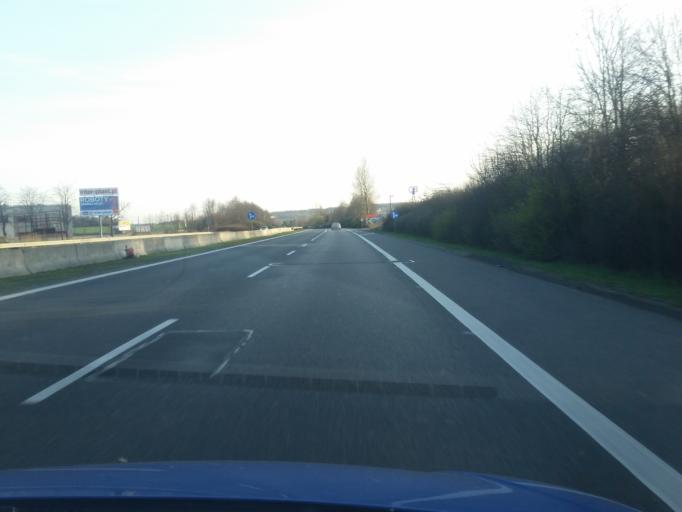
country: PL
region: Silesian Voivodeship
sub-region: Powiat czestochowski
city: Redziny
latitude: 50.8734
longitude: 19.1590
